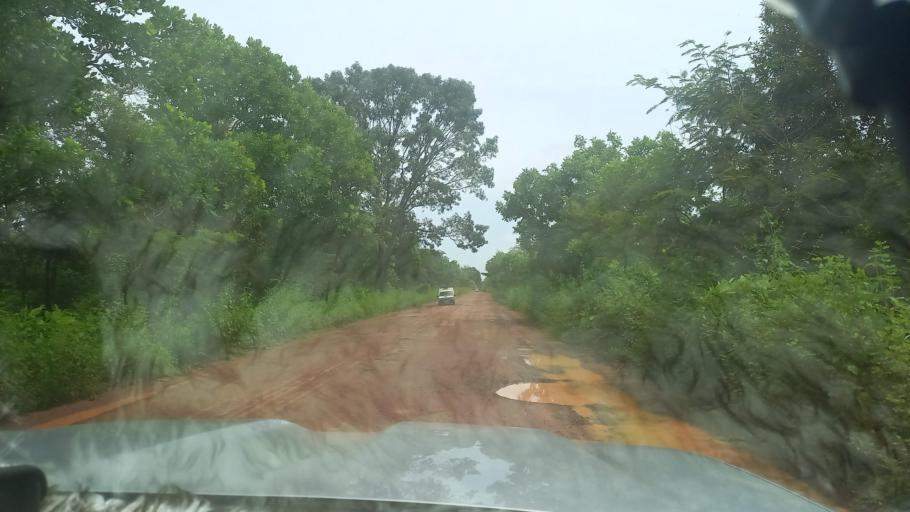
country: SN
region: Kolda
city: Marsassoum
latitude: 12.9024
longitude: -16.0240
